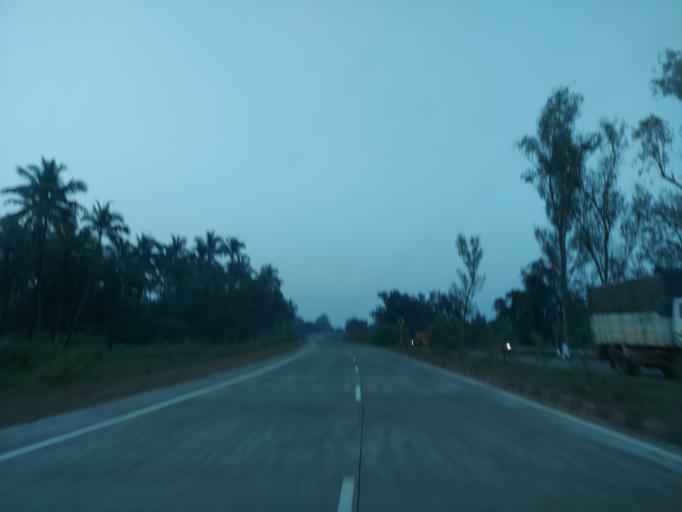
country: IN
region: Maharashtra
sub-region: Sindhudurg
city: Kudal
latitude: 16.0888
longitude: 73.7082
